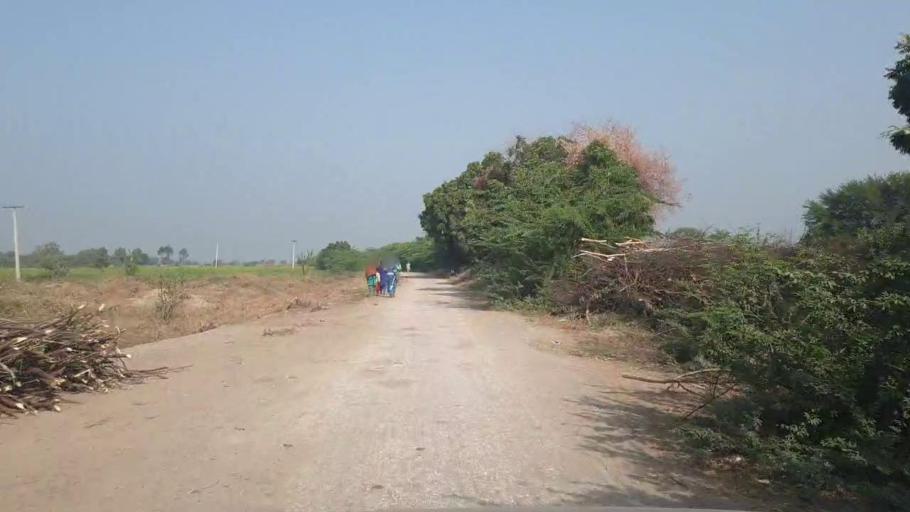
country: PK
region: Sindh
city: Umarkot
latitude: 25.3766
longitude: 69.7302
